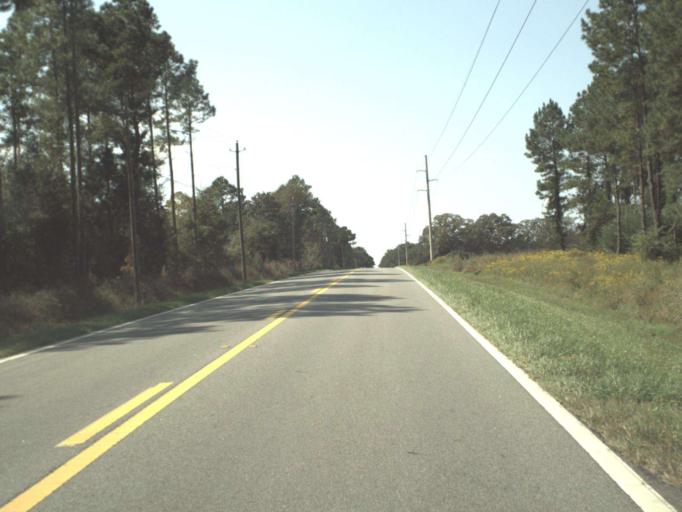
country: US
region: Florida
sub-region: Jackson County
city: Graceville
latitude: 30.9546
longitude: -85.4709
